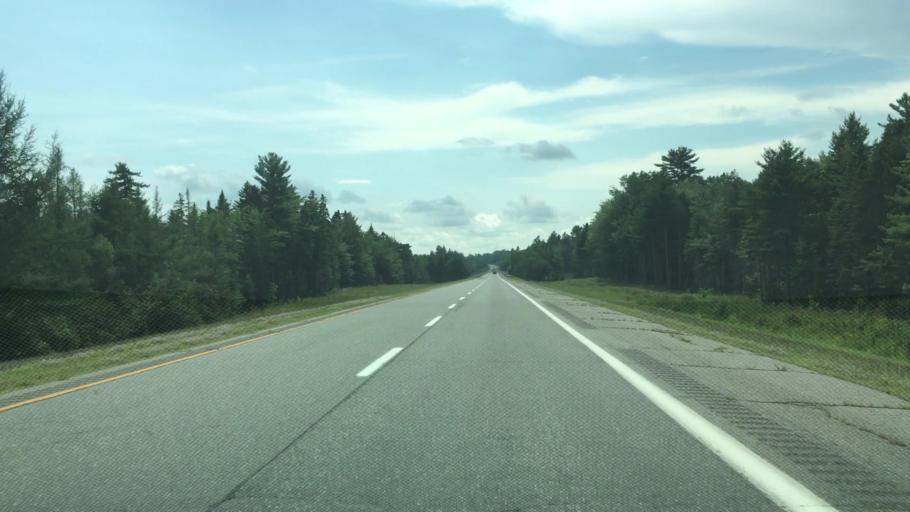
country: US
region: Maine
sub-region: Penobscot County
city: Lincoln
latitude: 45.4742
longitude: -68.5787
